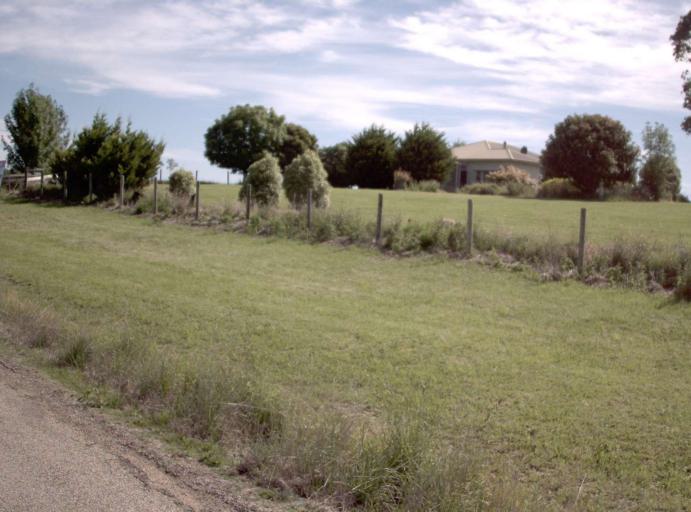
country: AU
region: Victoria
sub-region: East Gippsland
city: Lakes Entrance
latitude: -37.5016
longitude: 148.1329
